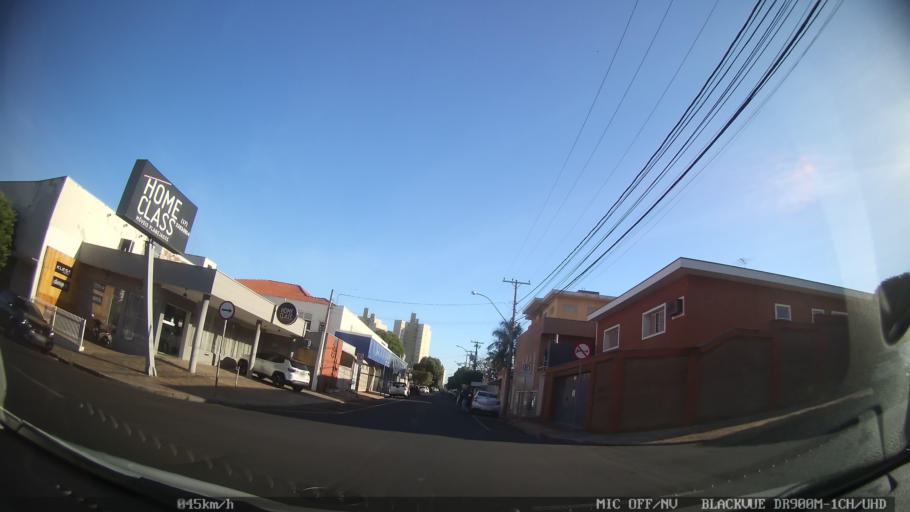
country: BR
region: Sao Paulo
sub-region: Sao Jose Do Rio Preto
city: Sao Jose do Rio Preto
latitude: -20.8129
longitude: -49.3918
